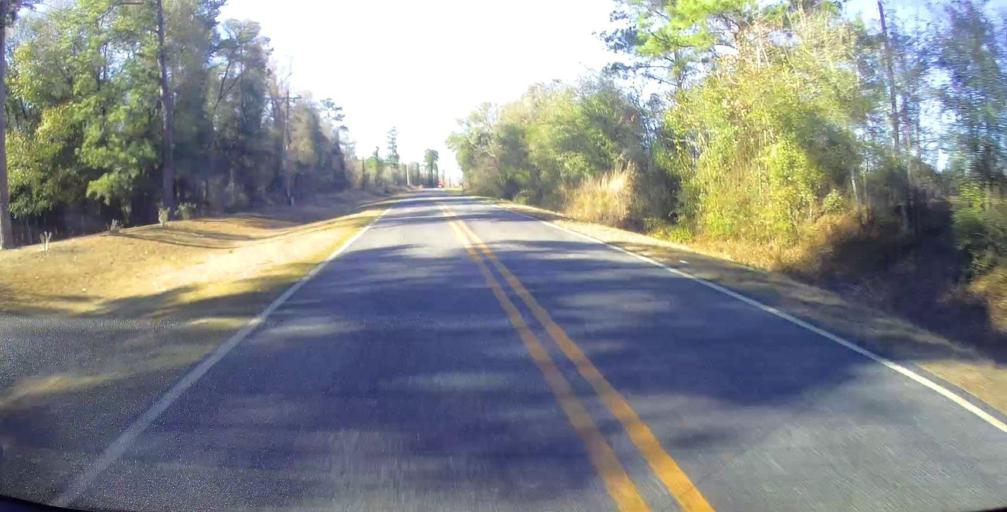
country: US
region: Georgia
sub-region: Peach County
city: Fort Valley
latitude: 32.5913
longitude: -83.8520
